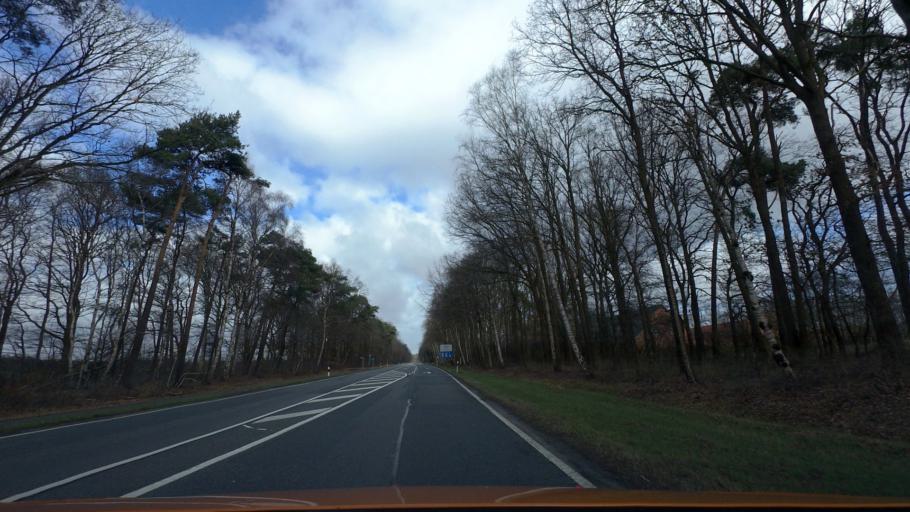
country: DE
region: Lower Saxony
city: Molbergen
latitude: 52.9256
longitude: 7.9511
